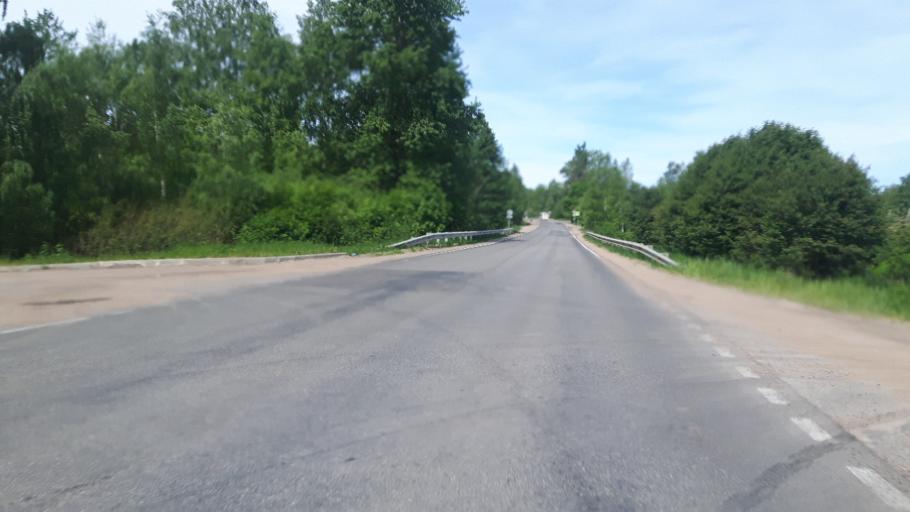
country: RU
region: Leningrad
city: Ust'-Luga
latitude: 59.6545
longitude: 28.2561
